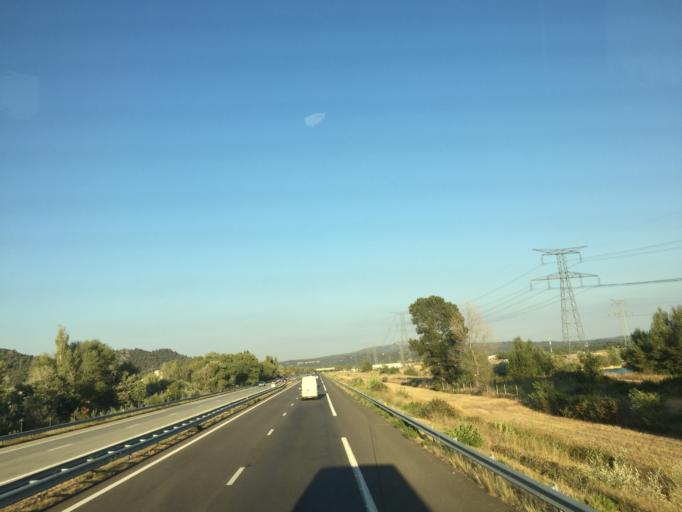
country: FR
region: Provence-Alpes-Cote d'Azur
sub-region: Departement des Bouches-du-Rhone
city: Peyrolles-en-Provence
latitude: 43.6586
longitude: 5.5639
